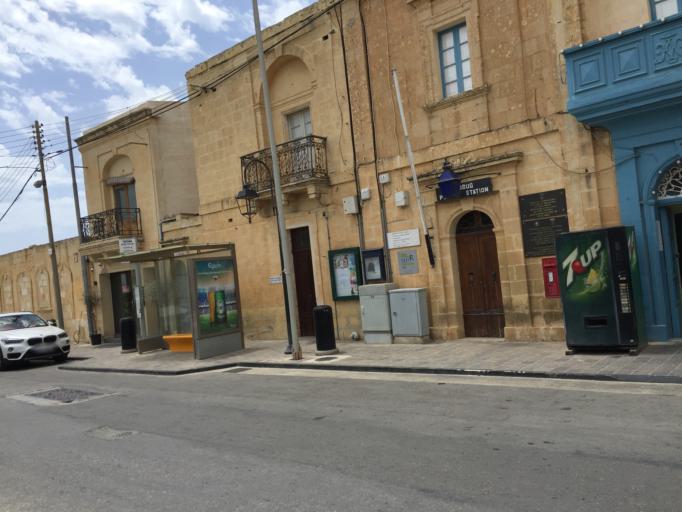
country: MT
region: Iz-Zebbug
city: Zebbug
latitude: 36.0694
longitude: 14.2357
